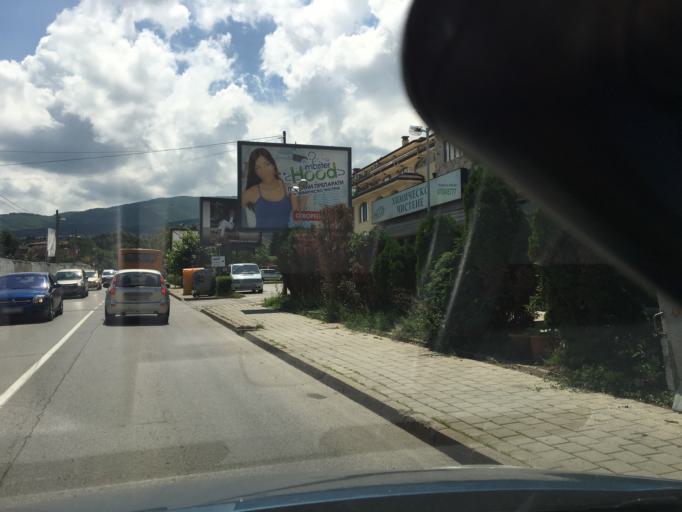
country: BG
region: Sofia-Capital
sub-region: Stolichna Obshtina
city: Sofia
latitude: 42.6307
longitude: 23.3334
